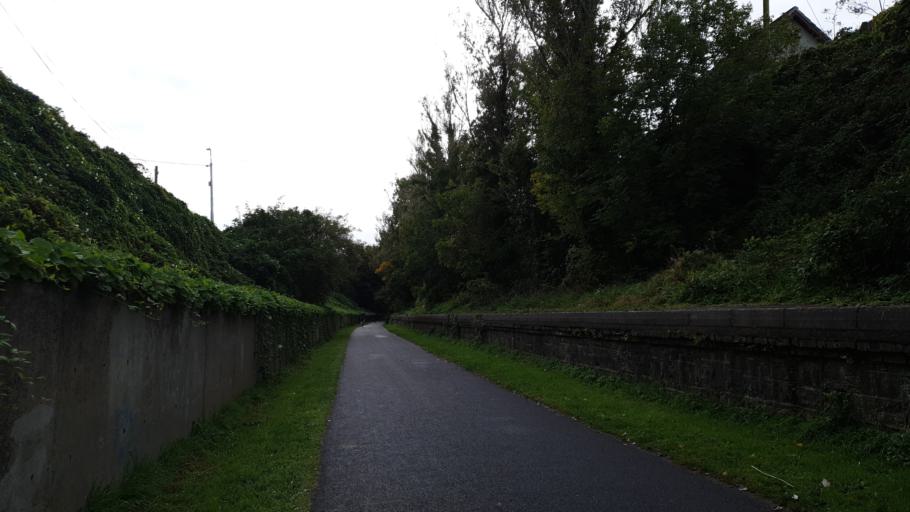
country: IE
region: Munster
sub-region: County Cork
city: Cork
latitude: 51.8961
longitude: -8.4185
